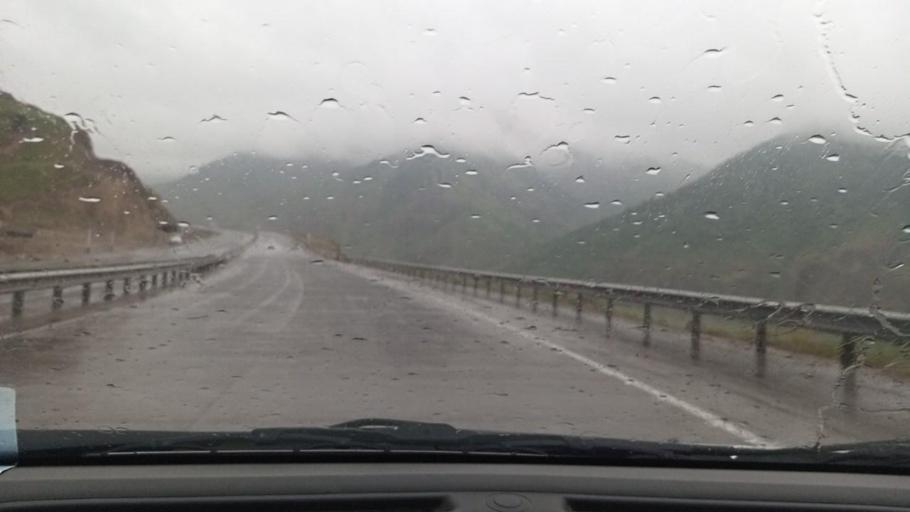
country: UZ
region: Toshkent
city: Angren
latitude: 41.0724
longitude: 70.2706
